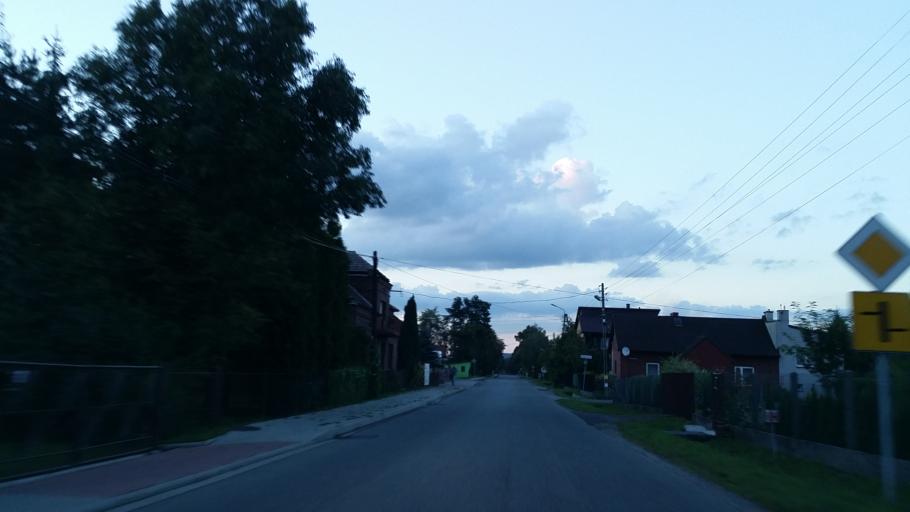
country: PL
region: Lesser Poland Voivodeship
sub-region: Powiat oswiecimski
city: Przeciszow
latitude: 50.0195
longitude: 19.3736
